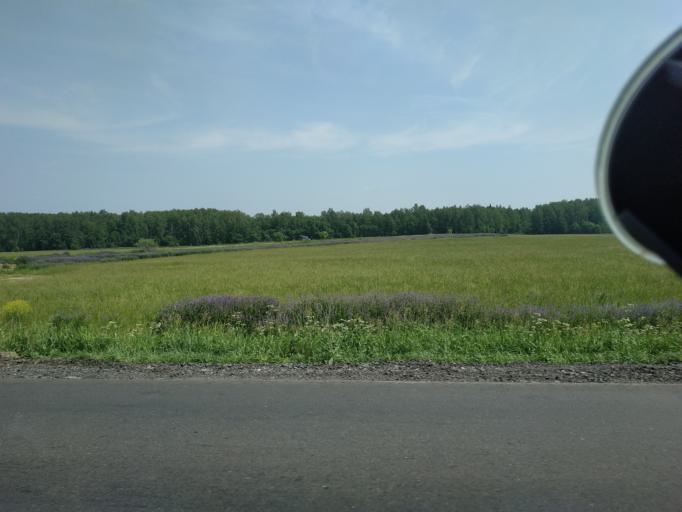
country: RU
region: Moskovskaya
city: Bronnitsy
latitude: 55.2947
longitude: 38.2127
